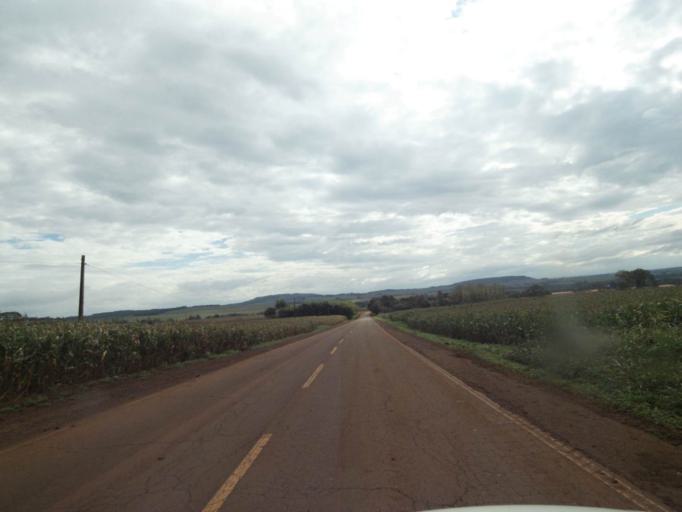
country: BR
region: Parana
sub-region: Marechal Candido Rondon
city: Marechal Candido Rondon
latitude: -24.7922
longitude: -54.2277
